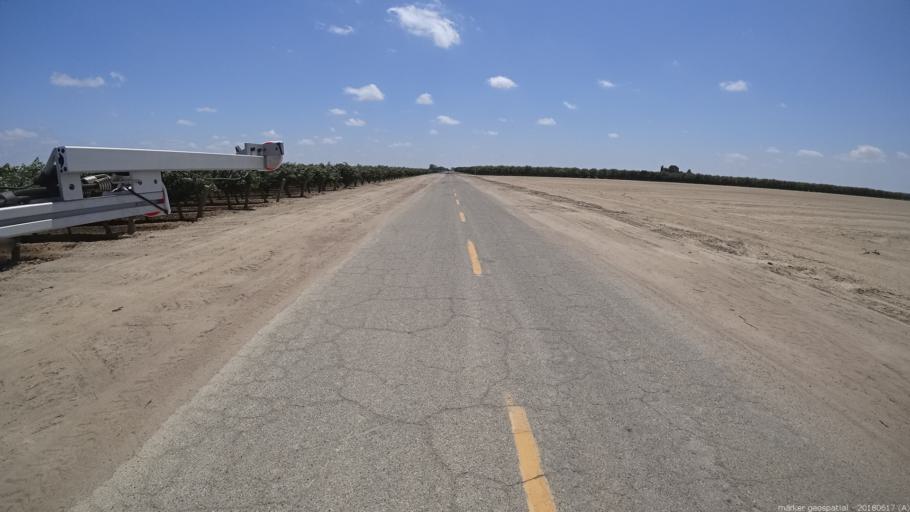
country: US
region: California
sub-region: Fresno County
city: Biola
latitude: 36.8309
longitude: -120.1330
